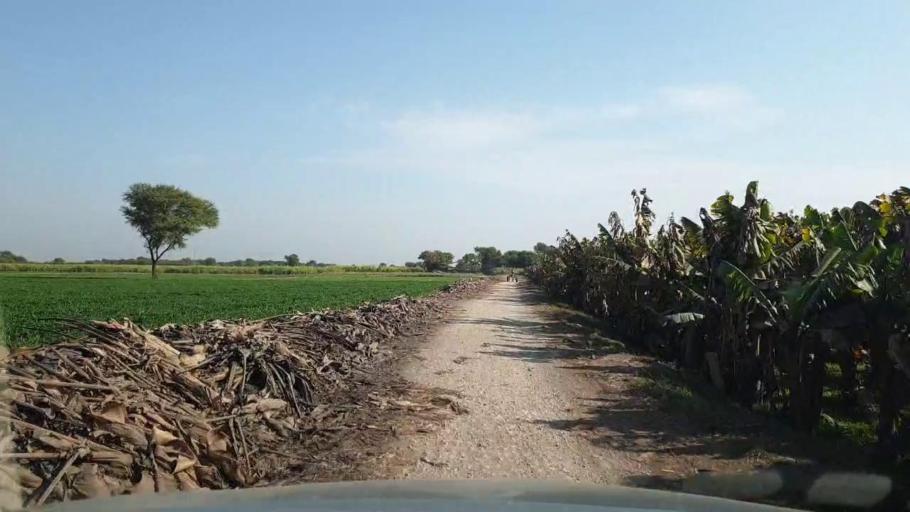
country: PK
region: Sindh
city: Tando Allahyar
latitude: 25.5781
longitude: 68.6095
